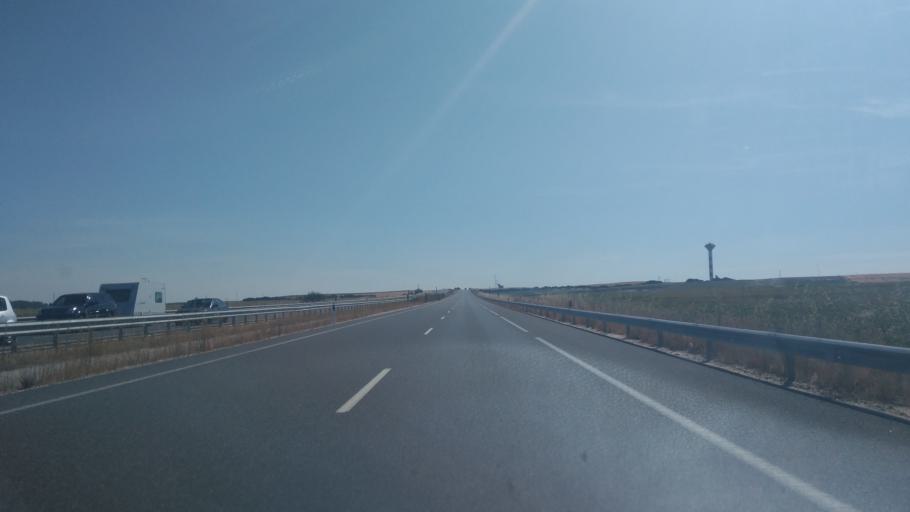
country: ES
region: Castille and Leon
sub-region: Provincia de Salamanca
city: Cordovilla
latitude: 40.9300
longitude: -5.4284
